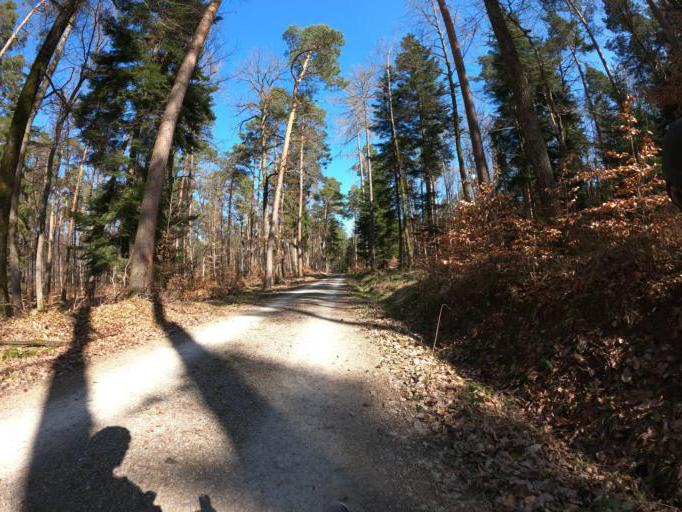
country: DE
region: Baden-Wuerttemberg
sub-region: Tuebingen Region
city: Rangendingen
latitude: 48.3942
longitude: 8.9224
